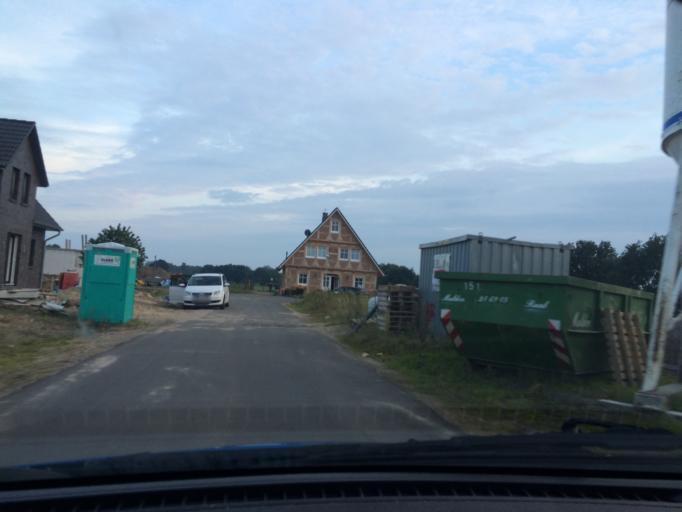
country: DE
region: Lower Saxony
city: Handorf
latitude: 53.3334
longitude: 10.3529
